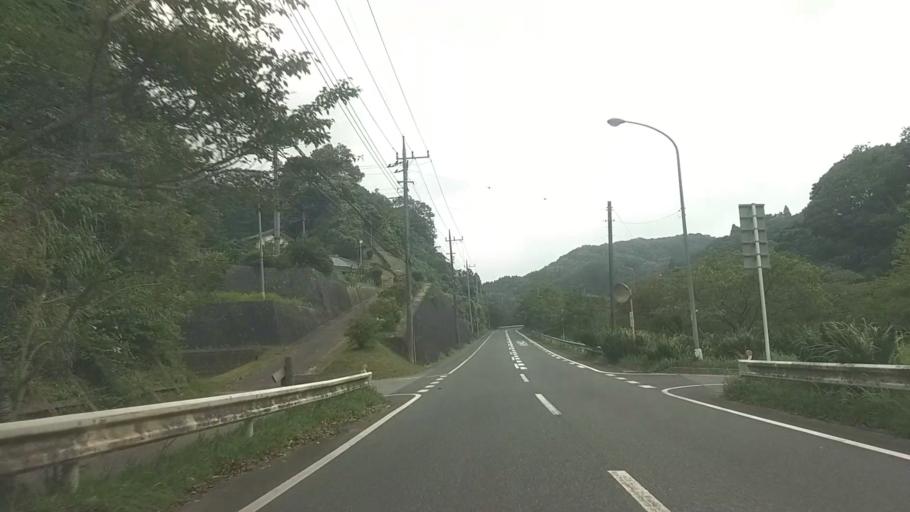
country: JP
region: Chiba
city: Kimitsu
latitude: 35.2337
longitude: 139.9682
